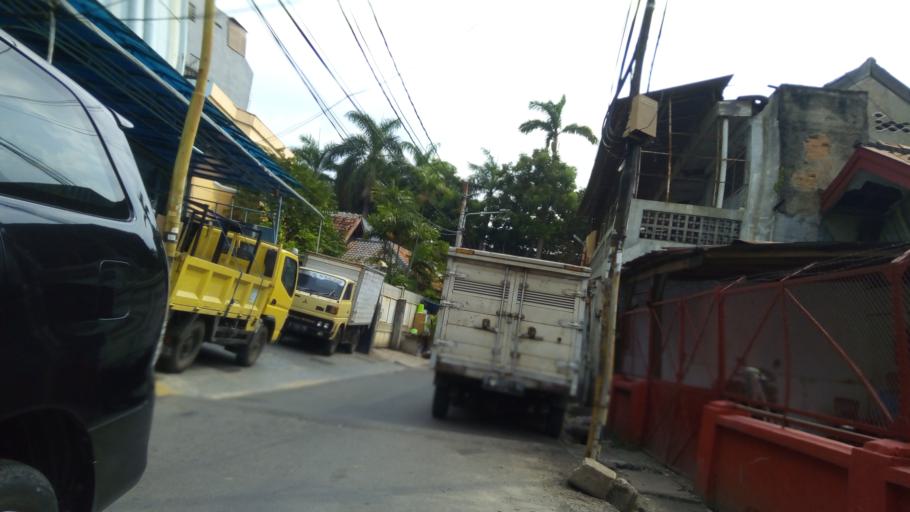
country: ID
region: Jakarta Raya
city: Jakarta
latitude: -6.1591
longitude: 106.8346
